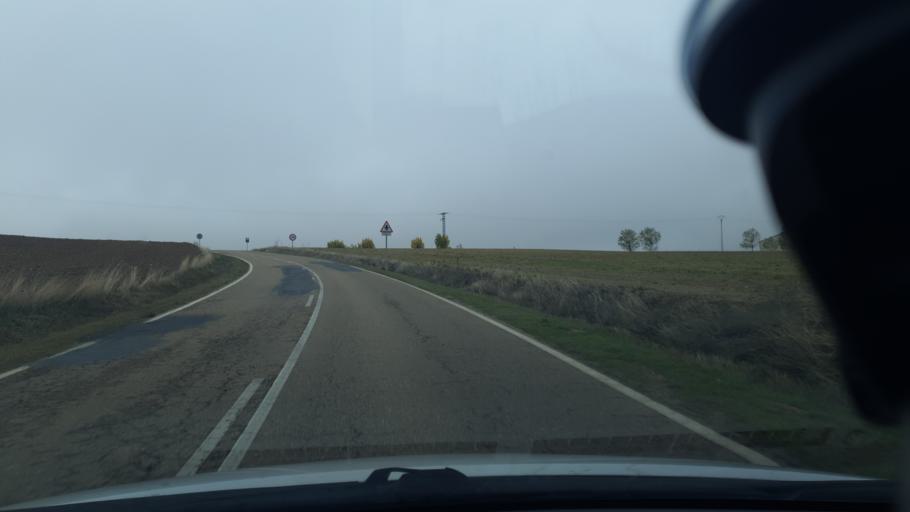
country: ES
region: Castille and Leon
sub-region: Provincia de Segovia
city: Hontanares de Eresma
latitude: 40.9927
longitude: -4.1911
